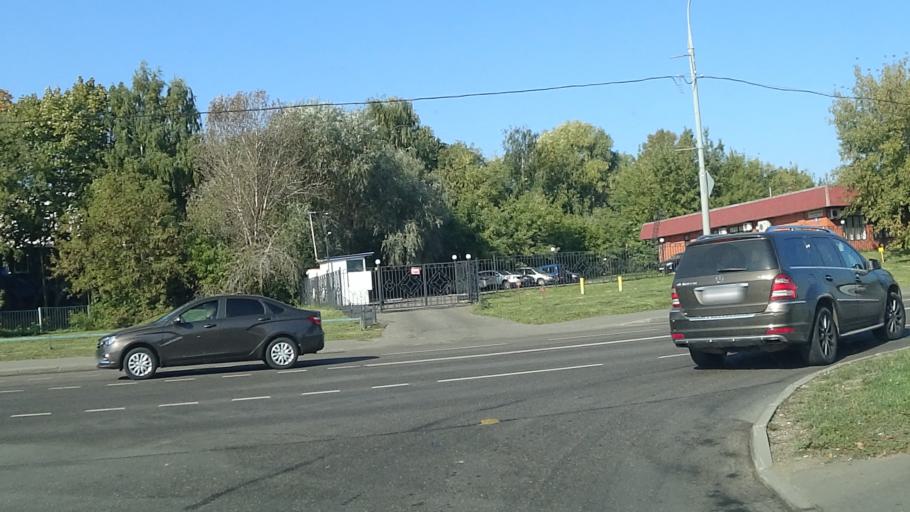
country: RU
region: Moskovskaya
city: Bol'shaya Setun'
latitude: 55.7536
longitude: 37.4328
